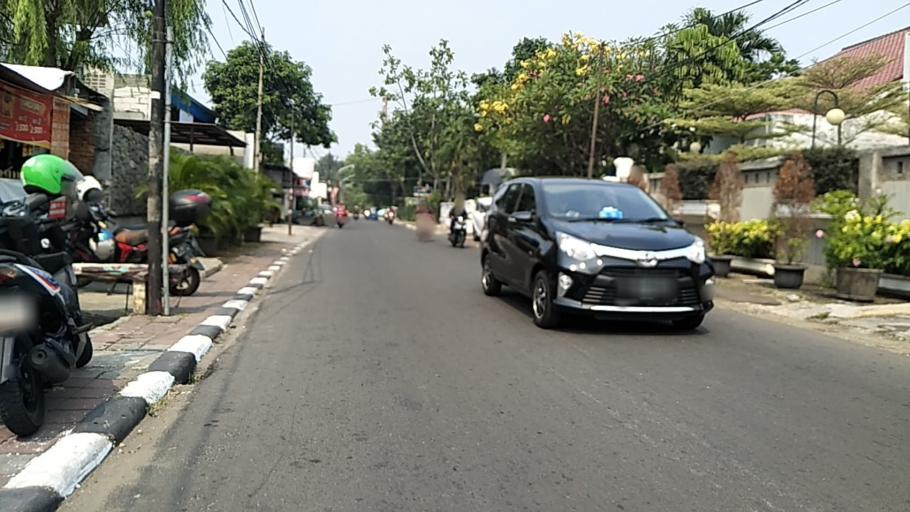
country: ID
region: Jakarta Raya
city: Jakarta
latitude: -6.2312
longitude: 106.8493
